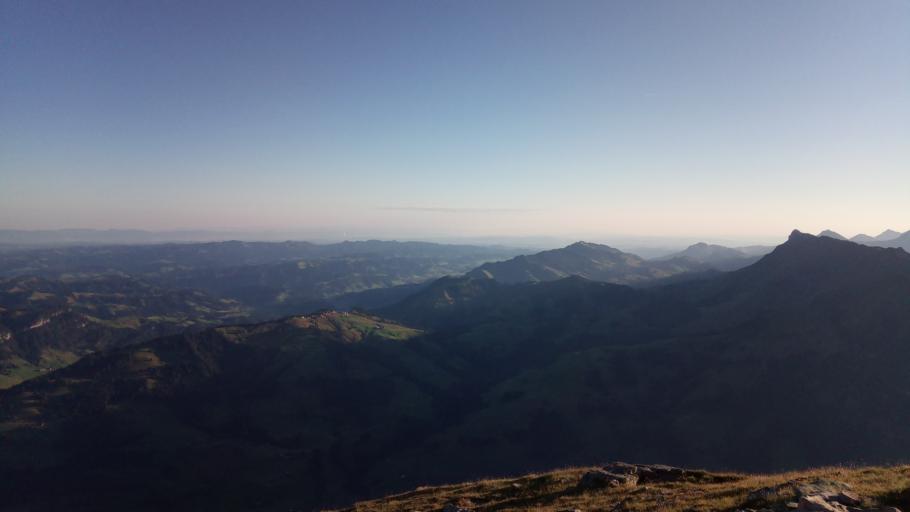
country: CH
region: Bern
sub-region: Emmental District
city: Wald
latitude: 46.7880
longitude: 7.9018
